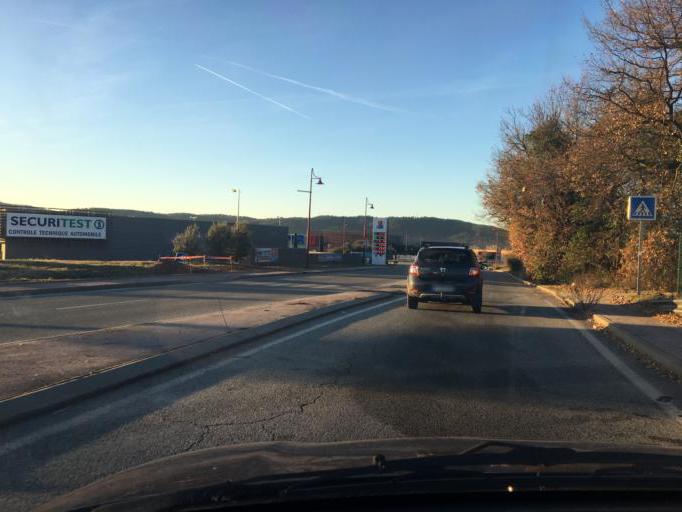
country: FR
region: Provence-Alpes-Cote d'Azur
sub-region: Departement du Var
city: Les Arcs
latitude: 43.4535
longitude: 6.4904
